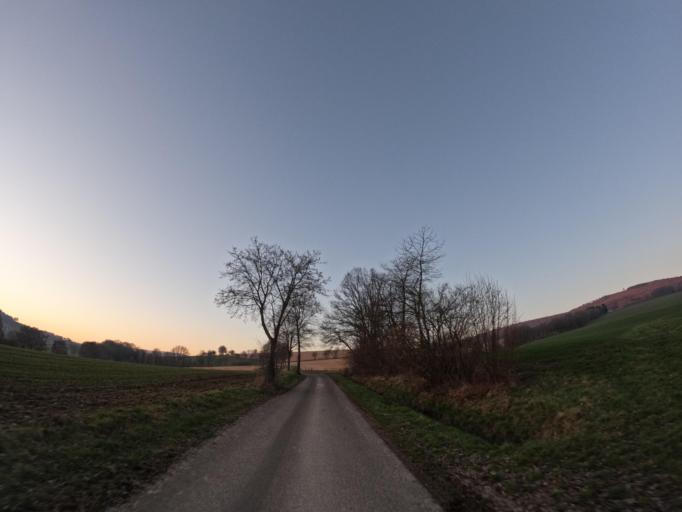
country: DE
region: Lower Saxony
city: Uslar
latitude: 51.6778
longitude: 9.5913
